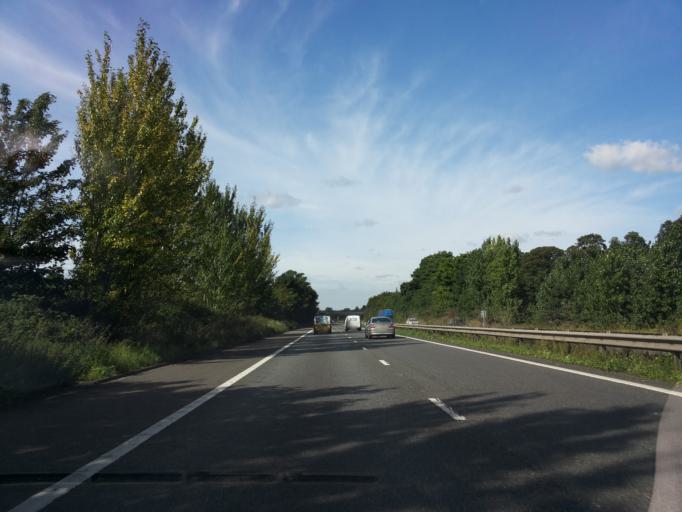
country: GB
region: England
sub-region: Kent
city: Sittingbourne
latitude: 51.3141
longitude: 0.7029
